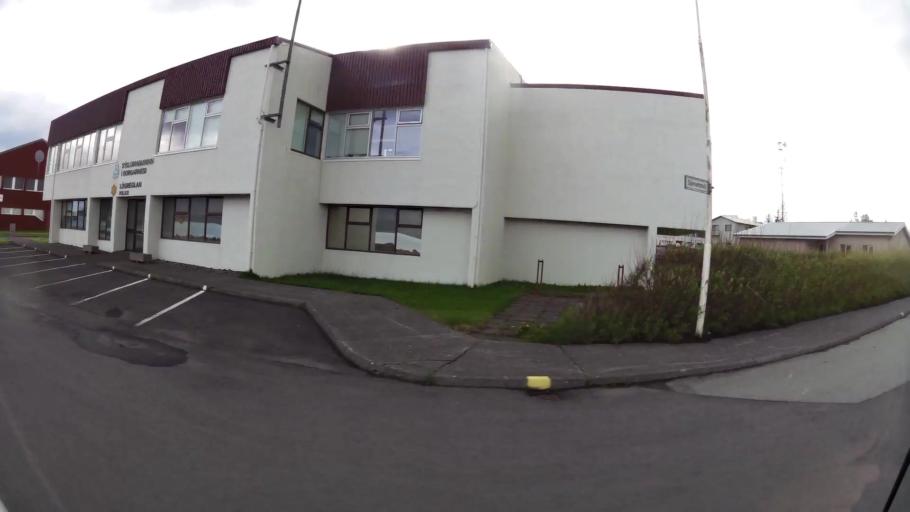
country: IS
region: West
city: Borgarnes
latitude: 64.5373
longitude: -21.9194
